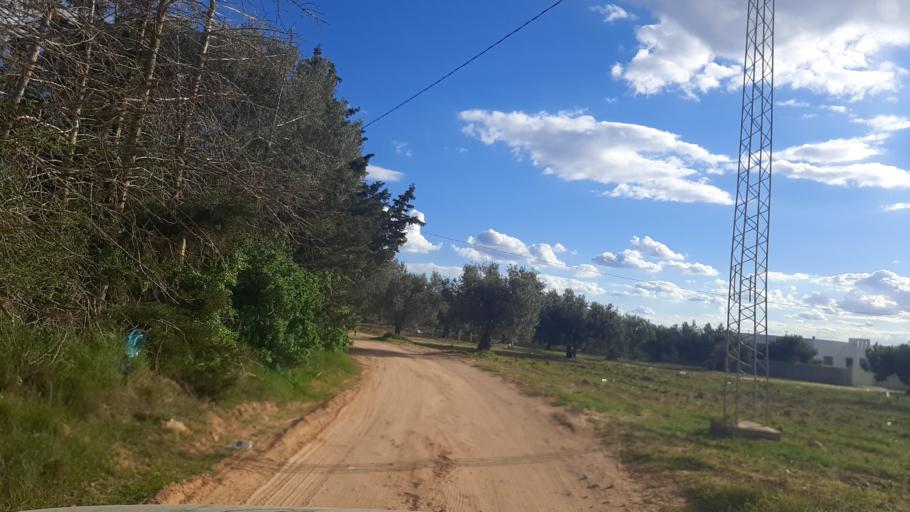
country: TN
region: Nabul
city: Al Hammamat
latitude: 36.4313
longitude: 10.5051
